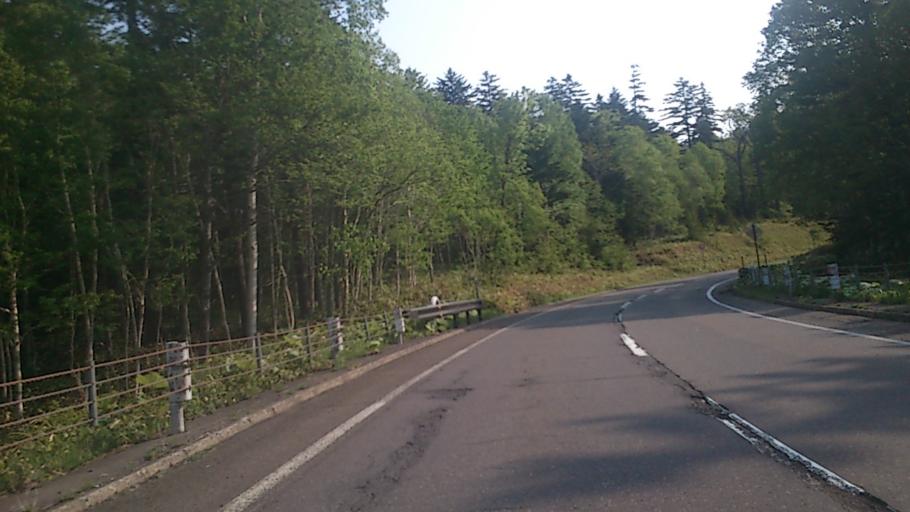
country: JP
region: Hokkaido
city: Bihoro
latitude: 43.4361
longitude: 144.1851
